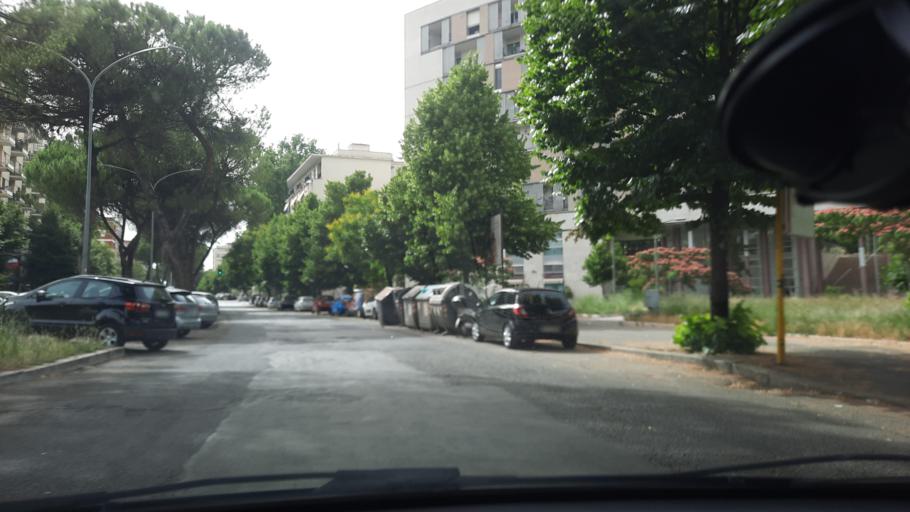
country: IT
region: Latium
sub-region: Citta metropolitana di Roma Capitale
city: Rome
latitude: 41.8557
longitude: 12.4862
